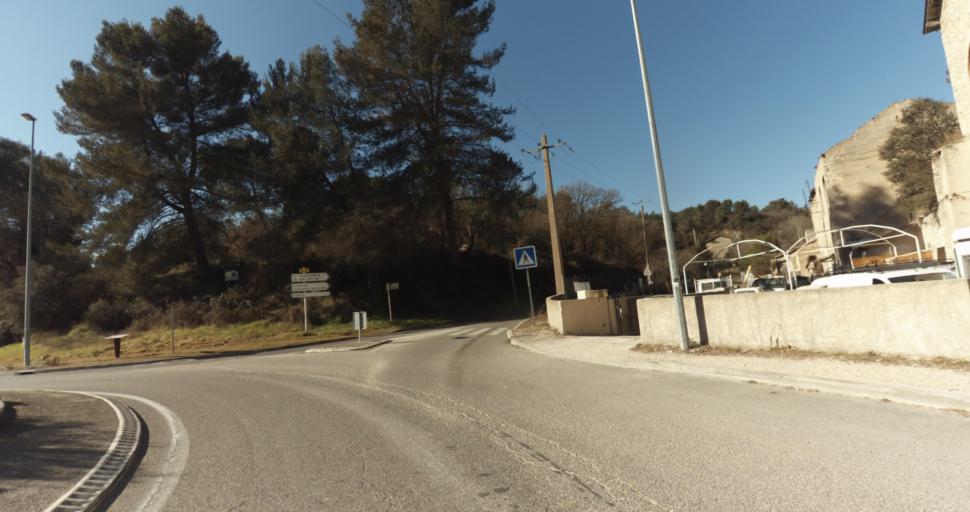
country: FR
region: Provence-Alpes-Cote d'Azur
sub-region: Departement des Bouches-du-Rhone
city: Cadolive
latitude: 43.4002
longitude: 5.5581
